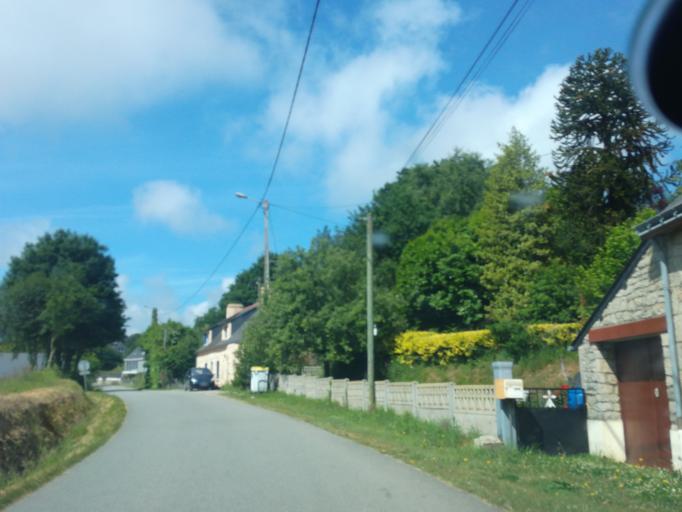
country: FR
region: Brittany
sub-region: Departement du Morbihan
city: Pontivy
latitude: 48.0787
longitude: -2.9391
